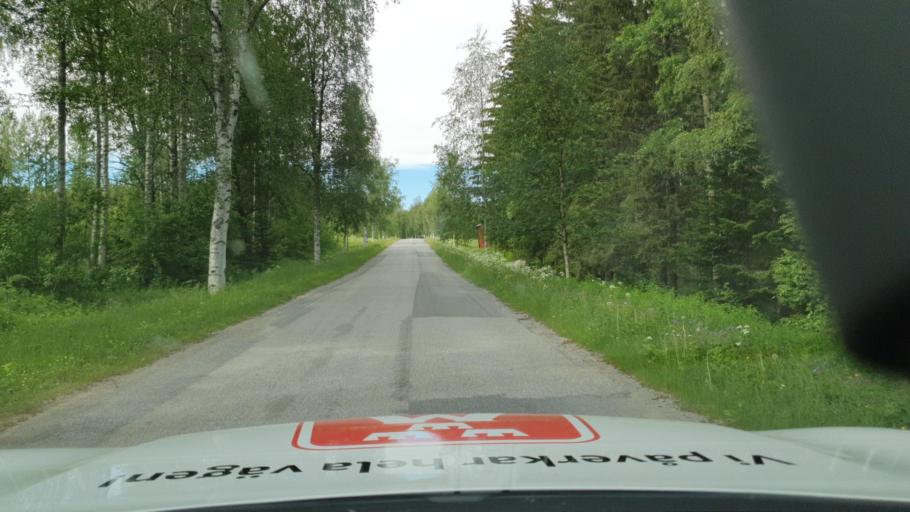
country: SE
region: Vaesterbotten
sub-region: Skelleftea Kommun
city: Burtraesk
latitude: 64.4321
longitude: 20.5163
